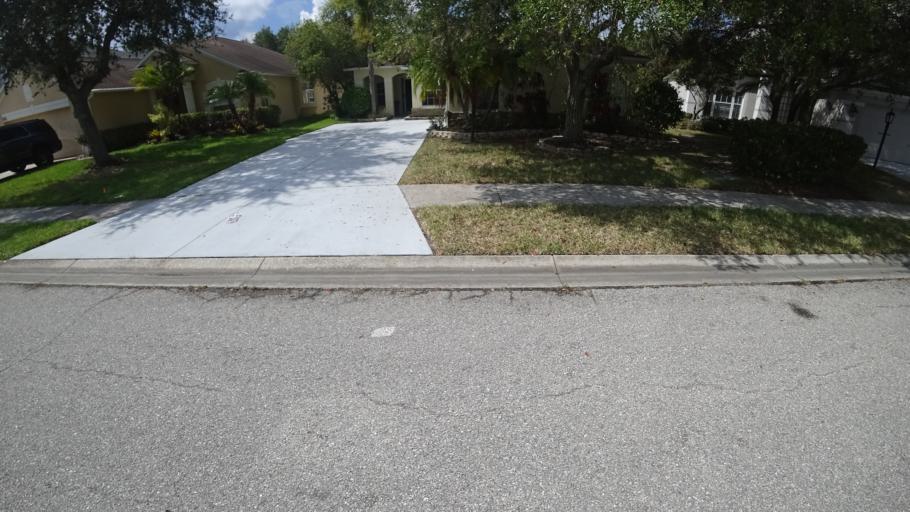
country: US
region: Florida
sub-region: Sarasota County
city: The Meadows
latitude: 27.4108
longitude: -82.4274
